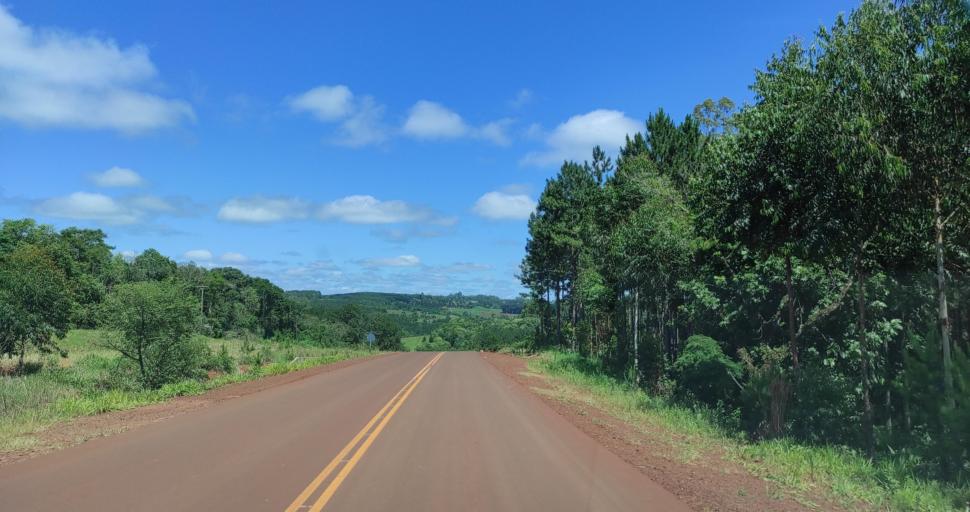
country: AR
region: Misiones
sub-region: Departamento de Veinticinco de Mayo
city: Veinticinco de Mayo
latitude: -27.3713
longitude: -54.7584
